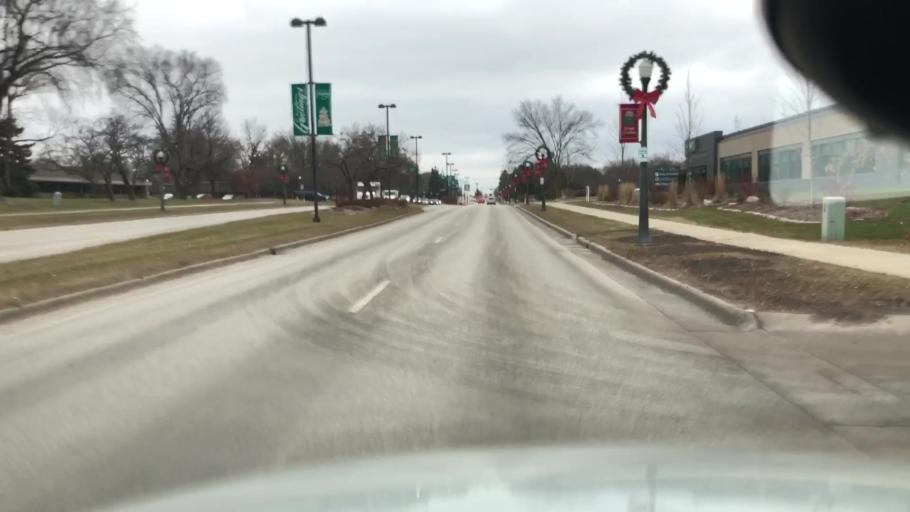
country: US
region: Wisconsin
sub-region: Waukesha County
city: Brookfield
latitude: 43.0571
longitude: -88.1264
